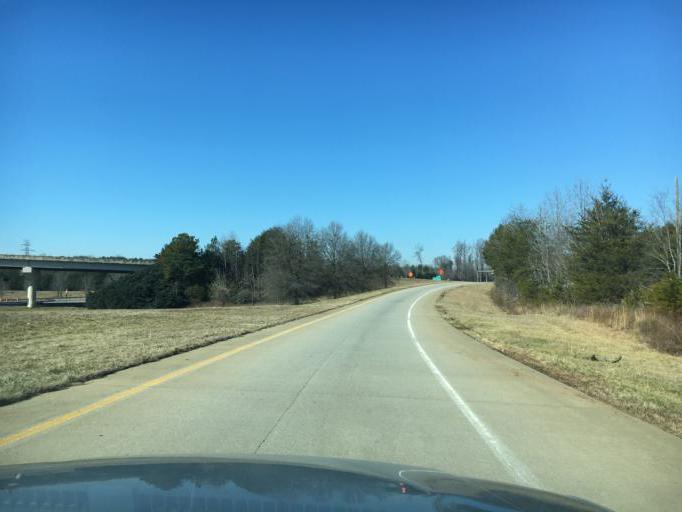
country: US
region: South Carolina
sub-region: Spartanburg County
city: Southern Shops
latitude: 34.9795
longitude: -82.0106
